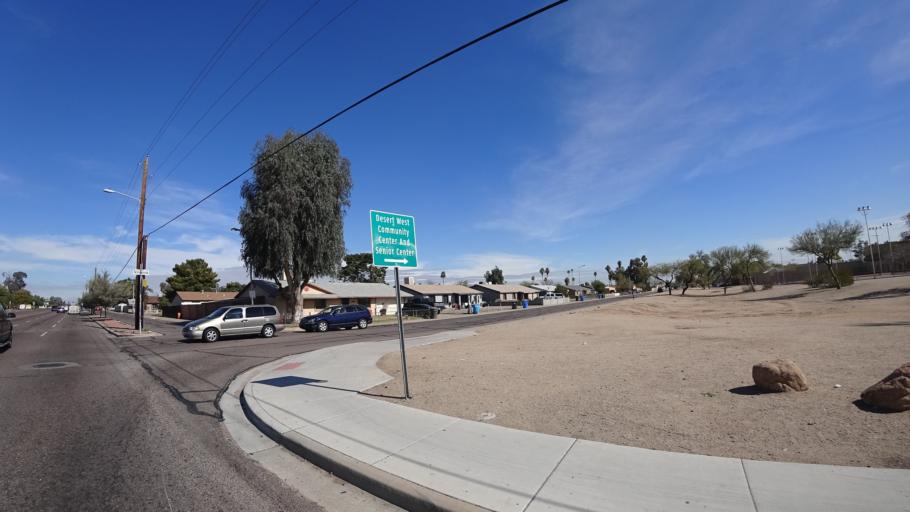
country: US
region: Arizona
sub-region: Maricopa County
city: Tolleson
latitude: 33.4764
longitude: -112.2032
